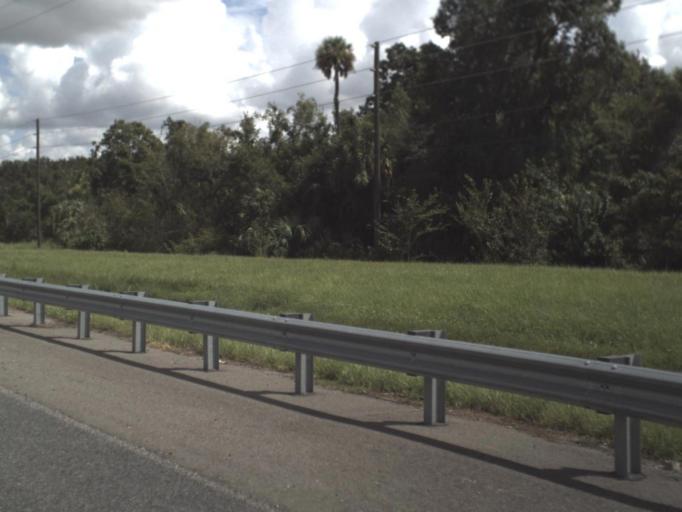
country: US
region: Florida
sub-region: Charlotte County
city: Harbour Heights
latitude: 27.0639
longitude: -81.9580
